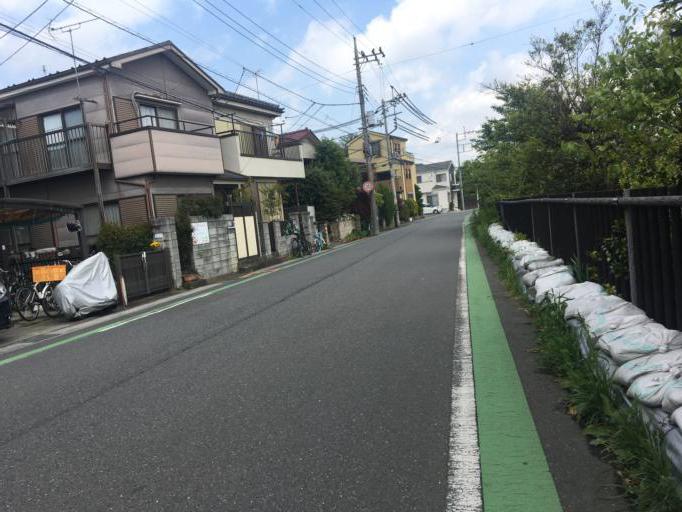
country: JP
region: Saitama
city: Kawagoe
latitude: 35.9031
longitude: 139.4932
